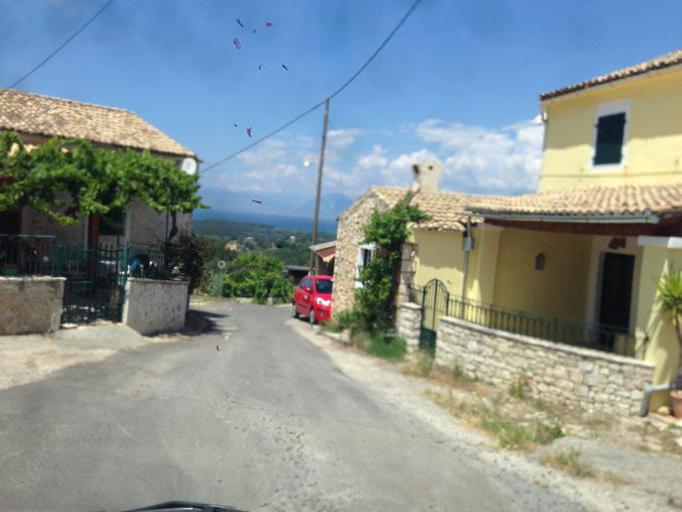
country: GR
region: Ionian Islands
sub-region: Nomos Kerkyras
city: Acharavi
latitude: 39.7978
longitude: 19.8532
